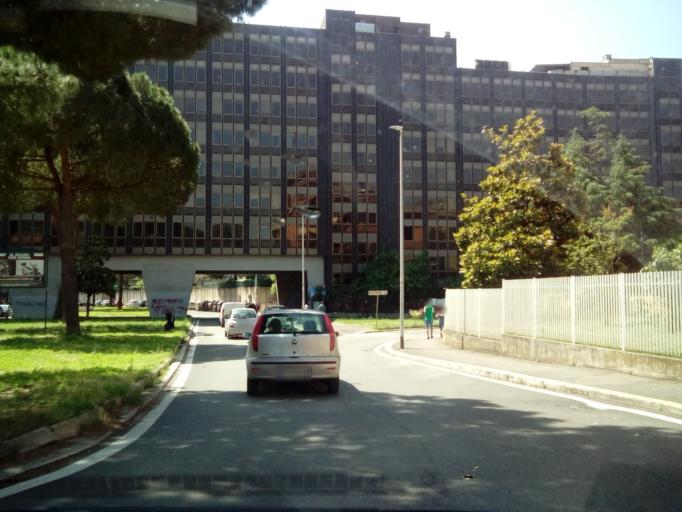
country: IT
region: Latium
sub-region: Citta metropolitana di Roma Capitale
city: Rome
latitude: 41.8834
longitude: 12.5890
